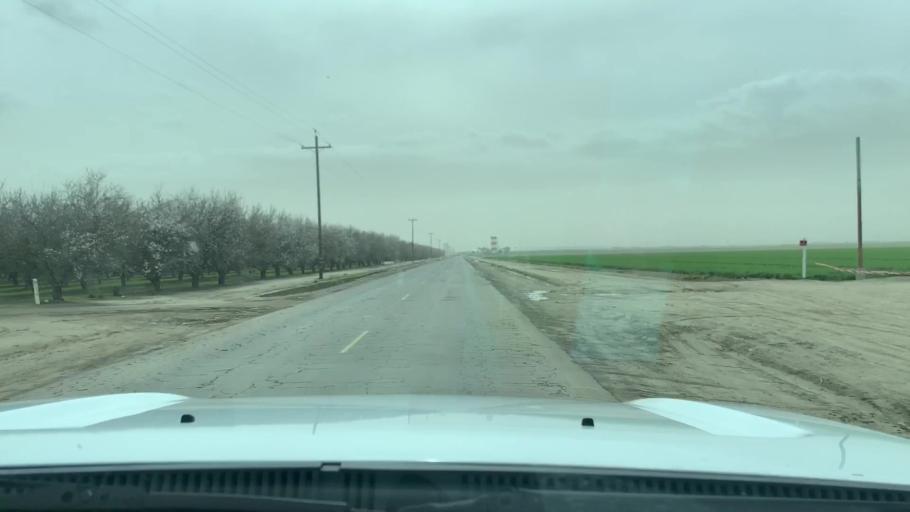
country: US
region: California
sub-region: Kern County
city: Wasco
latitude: 35.5652
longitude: -119.4028
